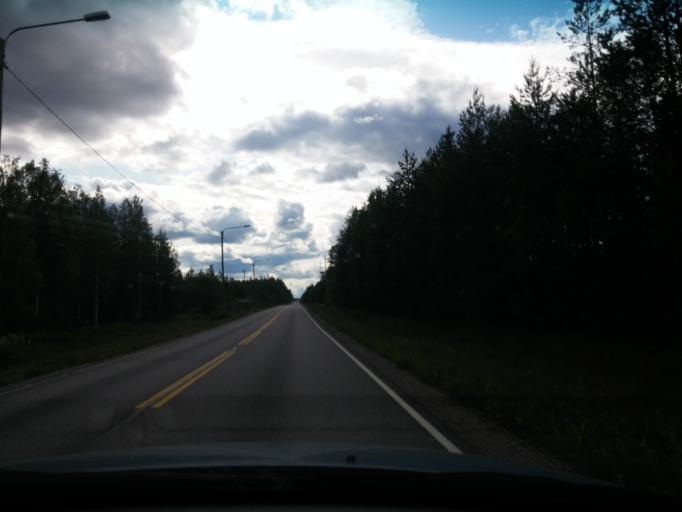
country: FI
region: Central Finland
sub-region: Saarijaervi-Viitasaari
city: Pylkoenmaeki
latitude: 62.6360
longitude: 24.8187
